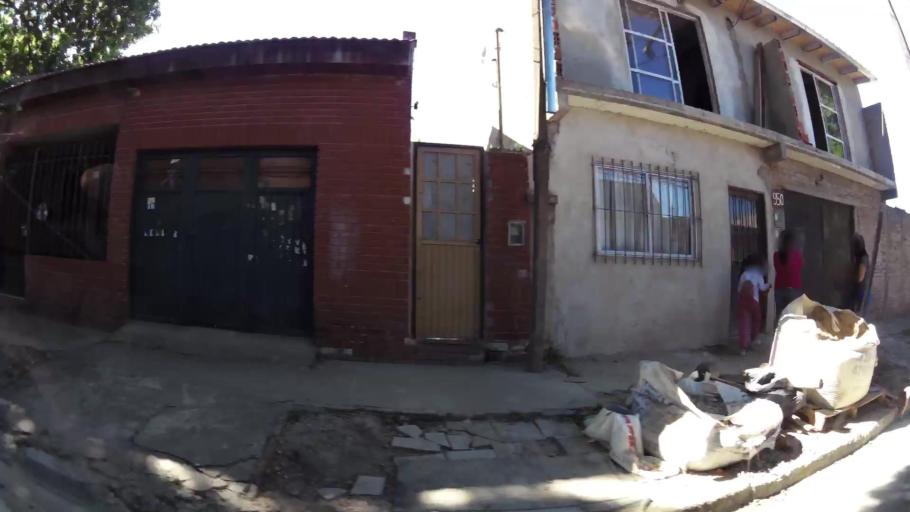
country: AR
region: Buenos Aires
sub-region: Partido de General San Martin
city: General San Martin
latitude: -34.5455
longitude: -58.5322
